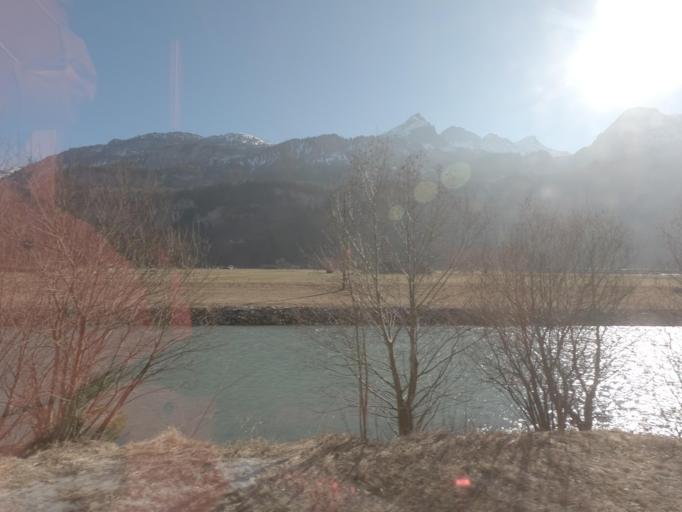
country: CH
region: Obwalden
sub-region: Obwalden
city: Lungern
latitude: 46.7445
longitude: 8.1291
